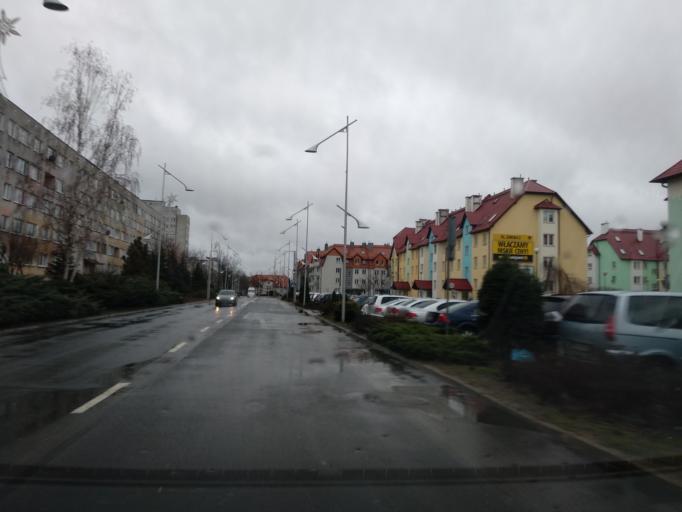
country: PL
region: Lower Silesian Voivodeship
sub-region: Powiat polkowicki
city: Polkowice
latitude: 51.5068
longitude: 16.0716
